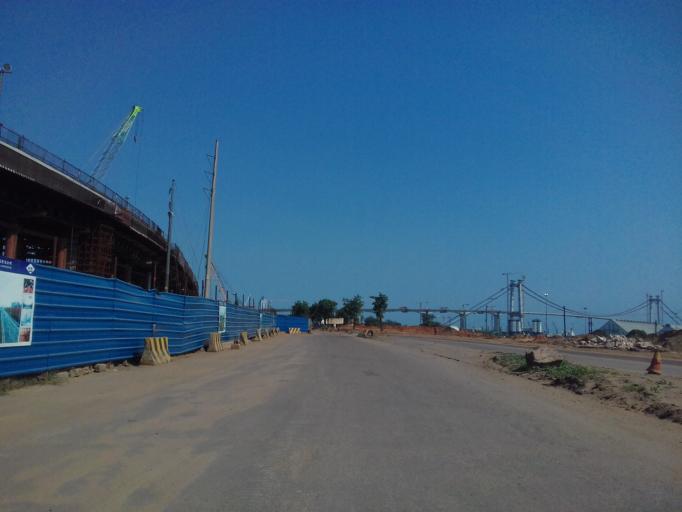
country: MZ
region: Maputo City
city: Maputo
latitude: -25.9559
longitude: 32.5526
